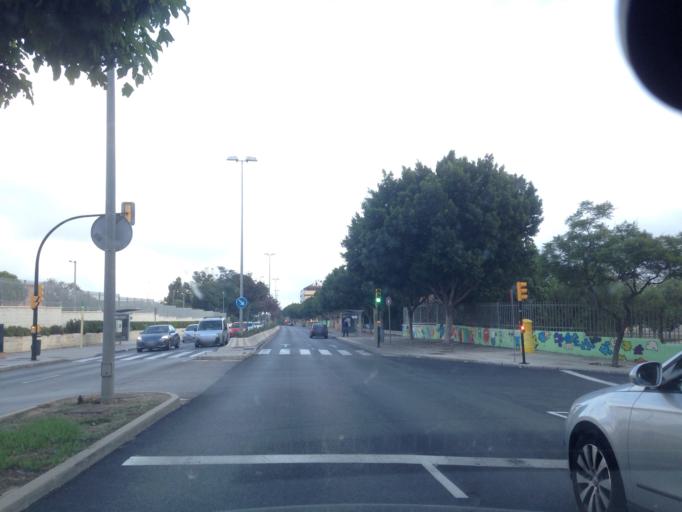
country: ES
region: Andalusia
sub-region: Provincia de Malaga
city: Malaga
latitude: 36.7299
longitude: -4.4672
